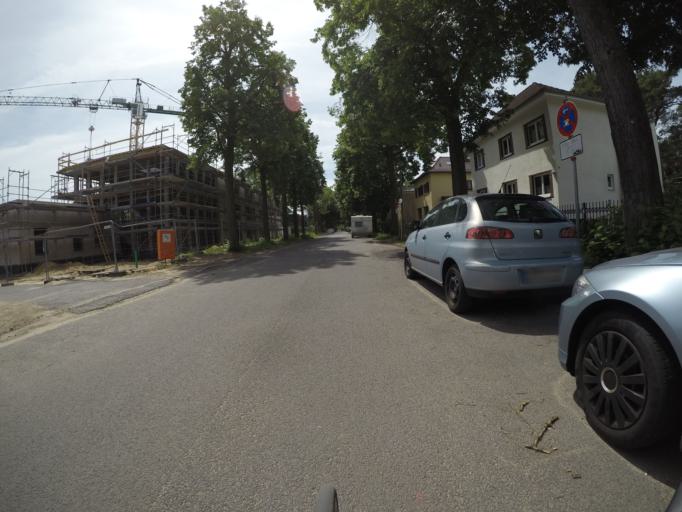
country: DE
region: Berlin
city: Kopenick Bezirk
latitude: 52.4498
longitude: 13.5627
